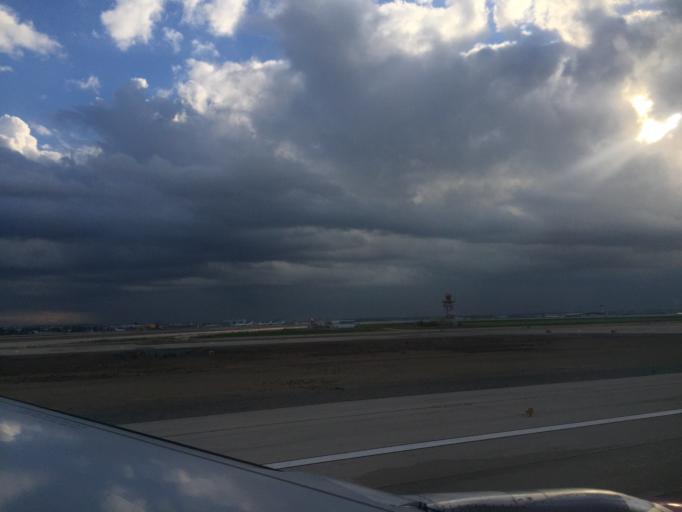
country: IL
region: Central District
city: Yehud
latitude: 32.0181
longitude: 34.8954
